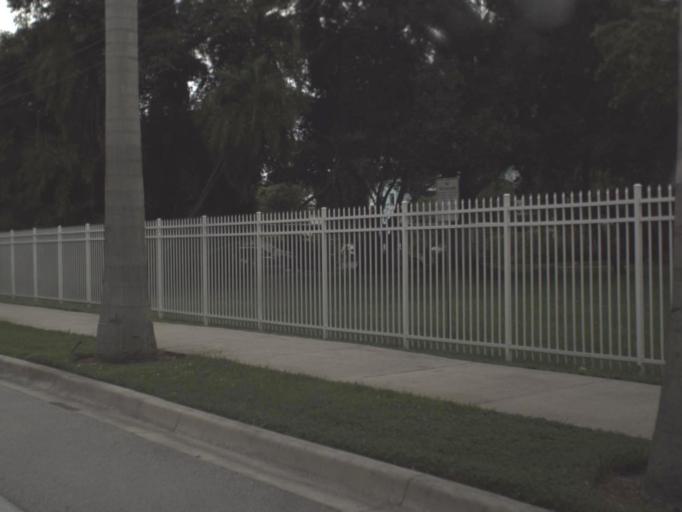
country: US
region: Florida
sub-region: Lee County
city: North Fort Myers
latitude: 26.6508
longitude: -81.8583
